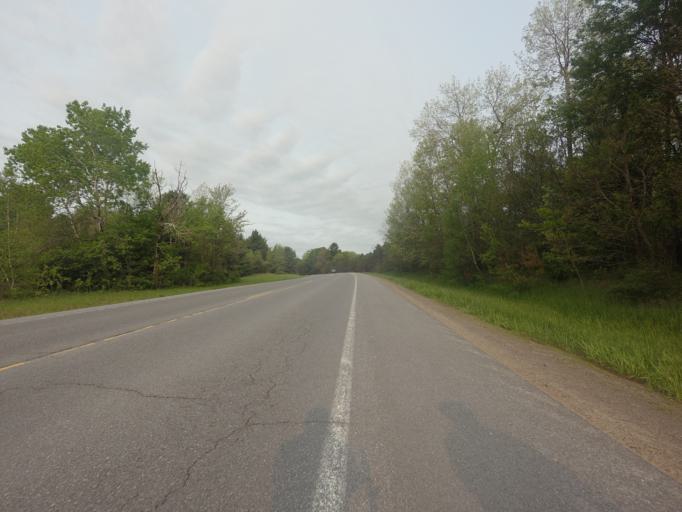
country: US
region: New York
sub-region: Jefferson County
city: Carthage
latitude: 44.0344
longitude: -75.6148
